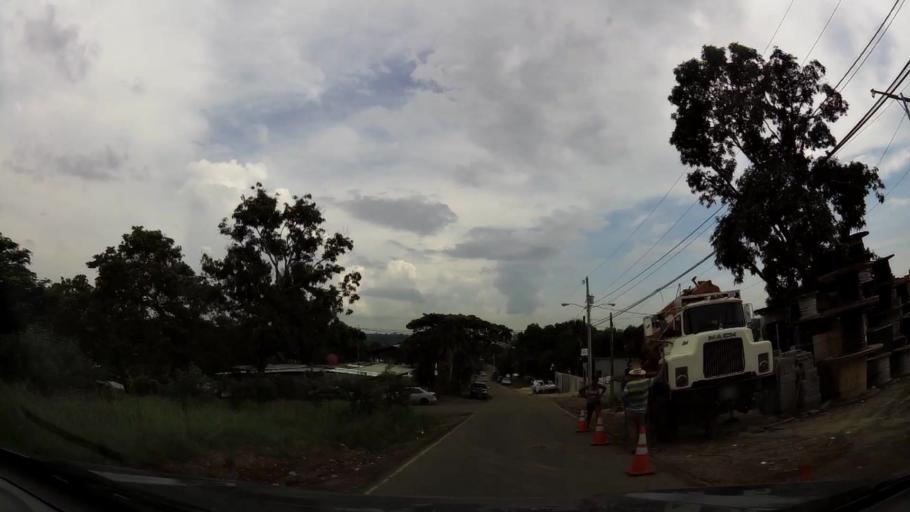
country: PA
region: Panama
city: Tocumen
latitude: 9.1149
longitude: -79.3740
